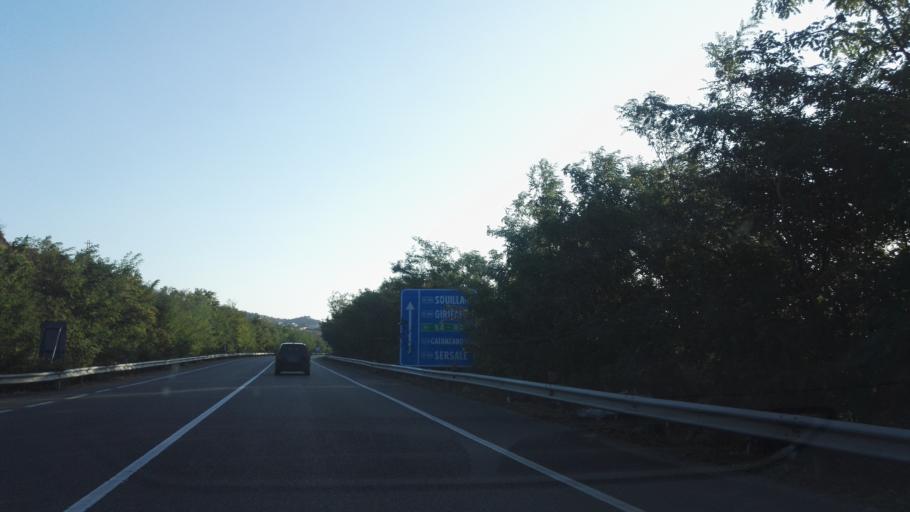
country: IT
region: Calabria
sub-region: Provincia di Catanzaro
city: Montepaone Lido
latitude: 38.7326
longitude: 16.5413
